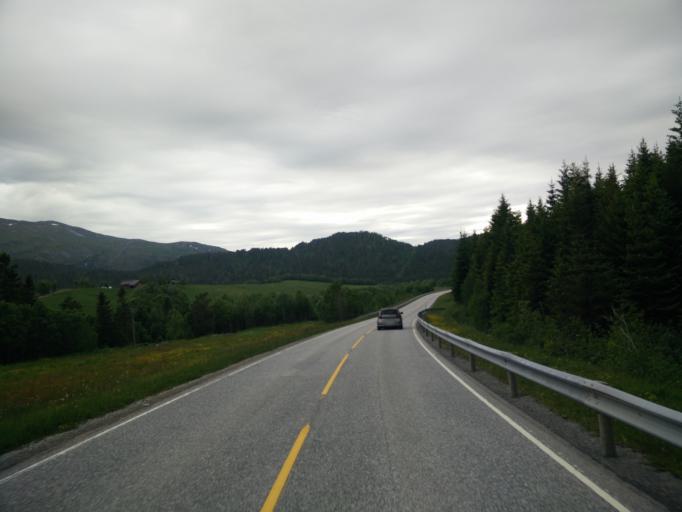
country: NO
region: Sor-Trondelag
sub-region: Hemne
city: Kyrksaeterora
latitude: 63.2082
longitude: 9.1710
